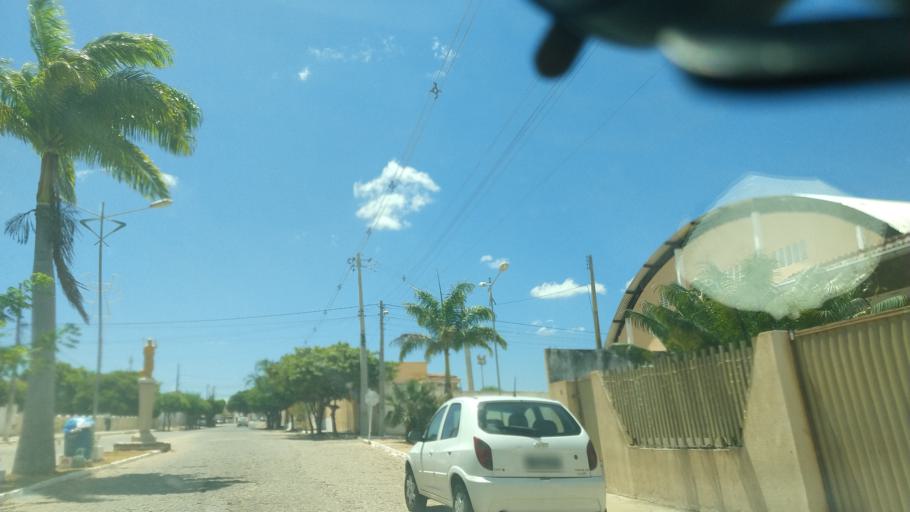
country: BR
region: Rio Grande do Norte
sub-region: Cerro Cora
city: Cerro Cora
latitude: -6.0497
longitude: -36.3522
